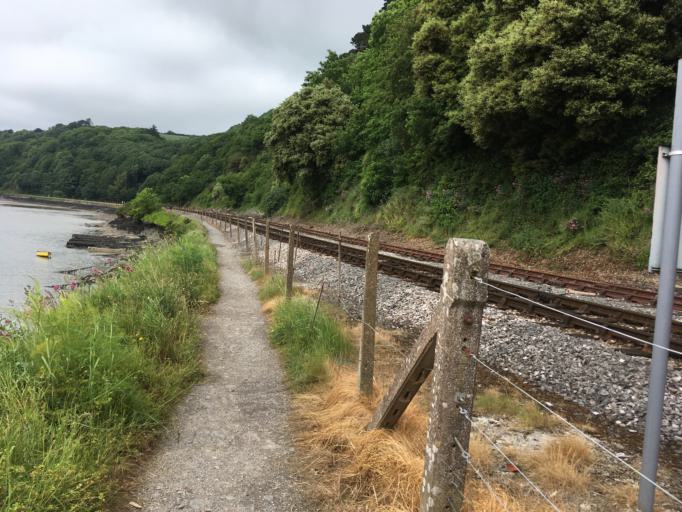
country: GB
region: England
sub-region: Devon
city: Dartmouth
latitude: 50.3531
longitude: -3.5702
